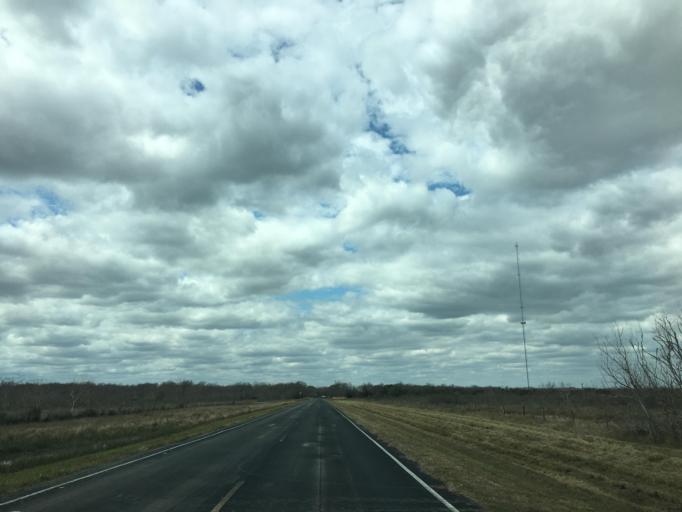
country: US
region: Texas
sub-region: Brazoria County
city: Oyster Creek
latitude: 29.0653
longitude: -95.3133
